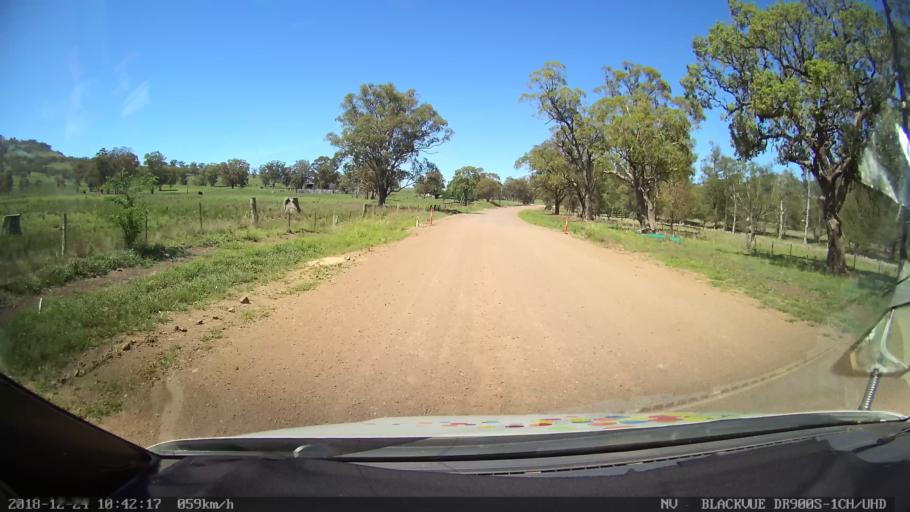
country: AU
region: New South Wales
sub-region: Upper Hunter Shire
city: Merriwa
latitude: -31.8754
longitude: 150.4540
